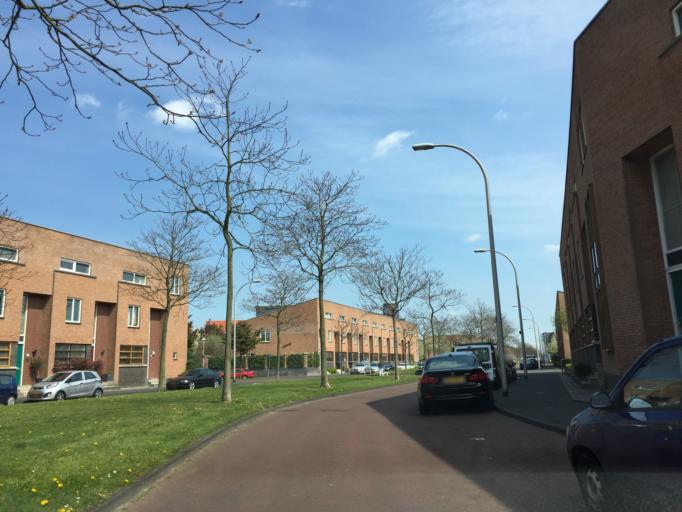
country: NL
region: South Holland
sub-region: Gemeente Den Haag
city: Ypenburg
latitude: 52.0489
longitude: 4.3779
